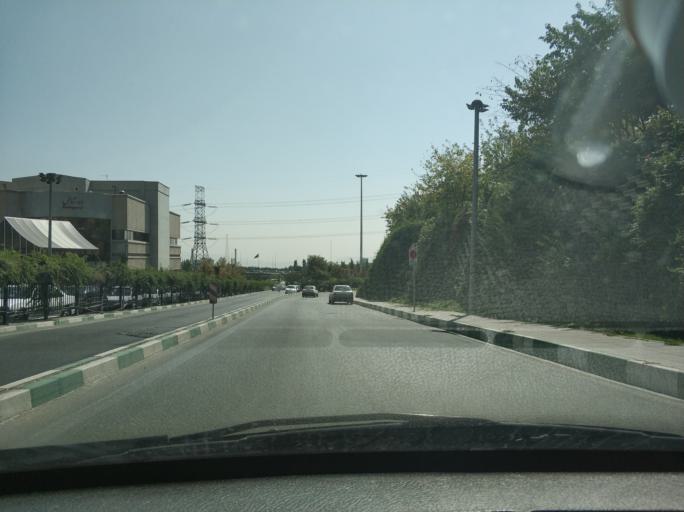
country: IR
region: Tehran
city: Tehran
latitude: 35.7454
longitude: 51.3796
